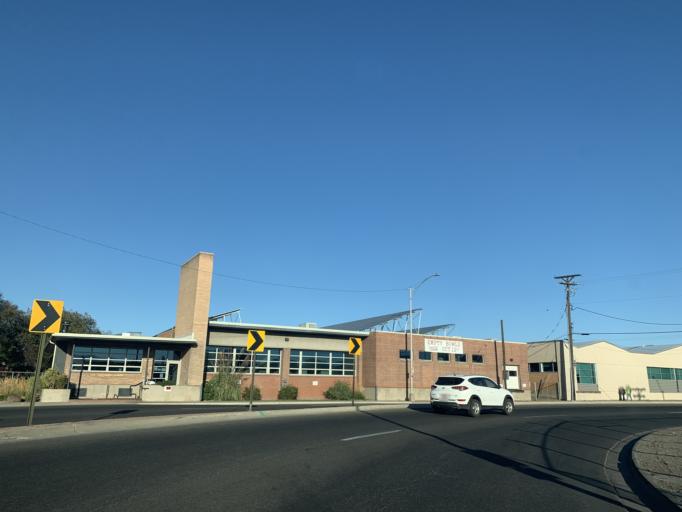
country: US
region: Colorado
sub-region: Mesa County
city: Grand Junction
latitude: 39.0654
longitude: -108.5707
